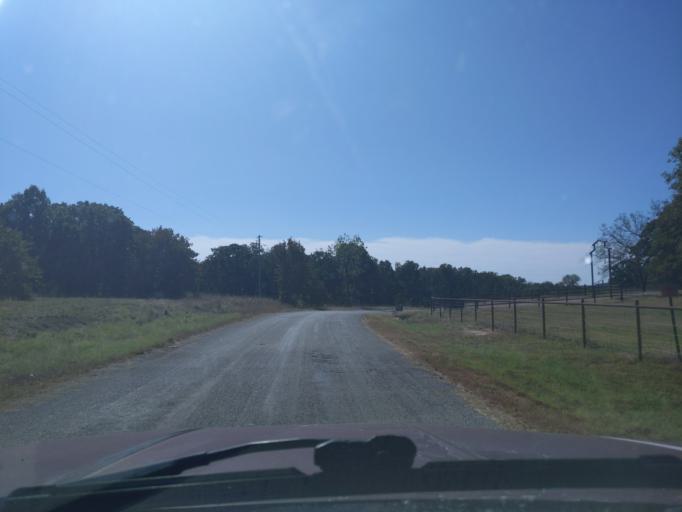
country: US
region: Oklahoma
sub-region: Creek County
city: Bristow
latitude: 35.6926
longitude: -96.4106
